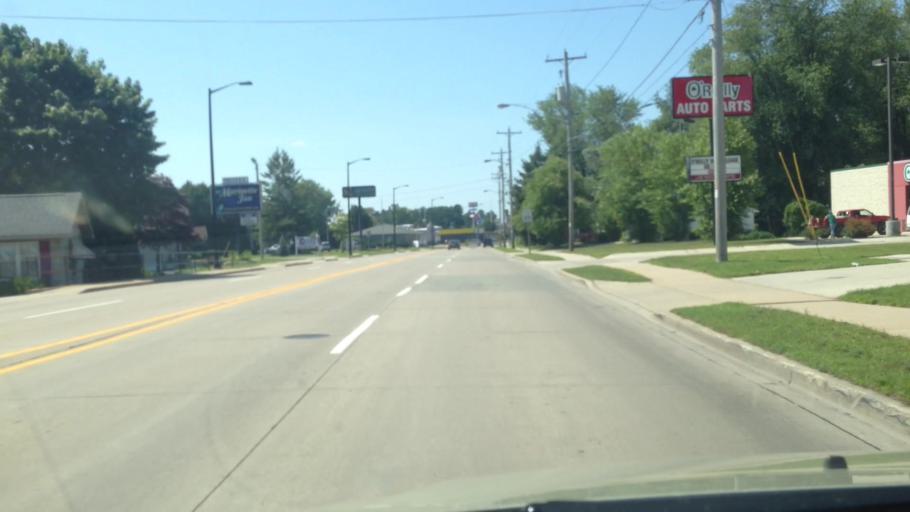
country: US
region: Wisconsin
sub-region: Marinette County
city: Marinette
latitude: 45.0918
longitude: -87.6484
